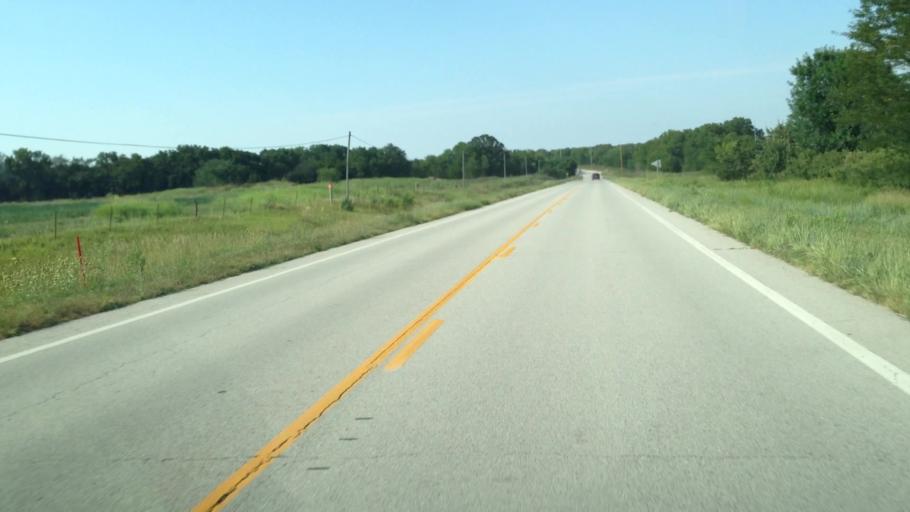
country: US
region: Kansas
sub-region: Allen County
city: Iola
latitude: 38.0336
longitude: -95.1731
